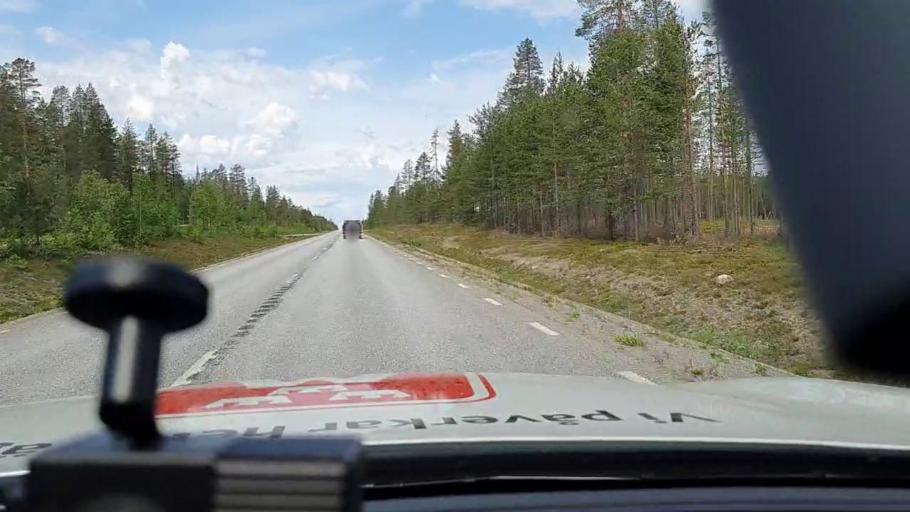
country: SE
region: Norrbotten
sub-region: Jokkmokks Kommun
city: Jokkmokk
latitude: 66.5229
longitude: 20.2062
